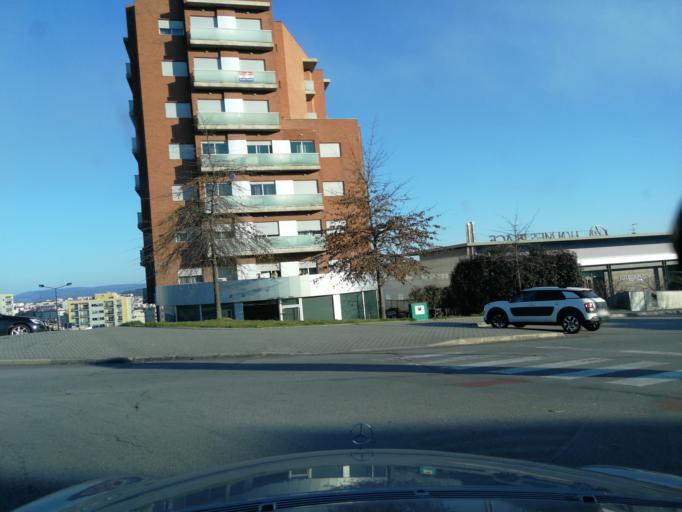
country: PT
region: Braga
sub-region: Braga
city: Braga
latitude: 41.5365
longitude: -8.4030
